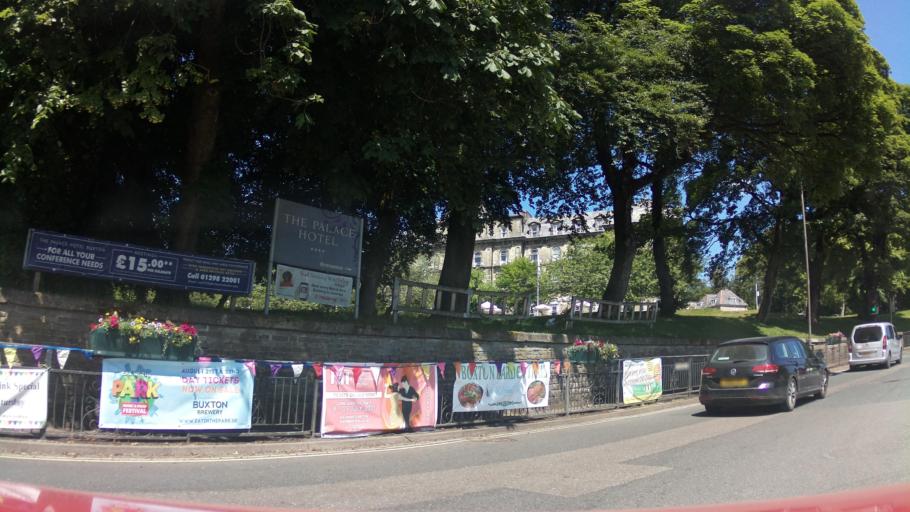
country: GB
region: England
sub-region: Derbyshire
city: Buxton
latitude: 53.2595
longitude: -1.9144
